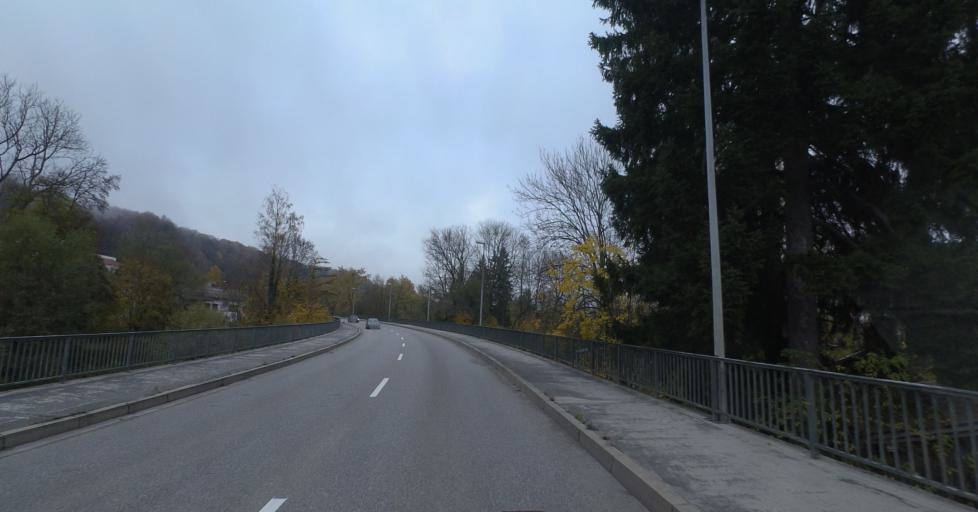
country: DE
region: Bavaria
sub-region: Upper Bavaria
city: Trostberg an der Alz
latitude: 48.0287
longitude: 12.5578
